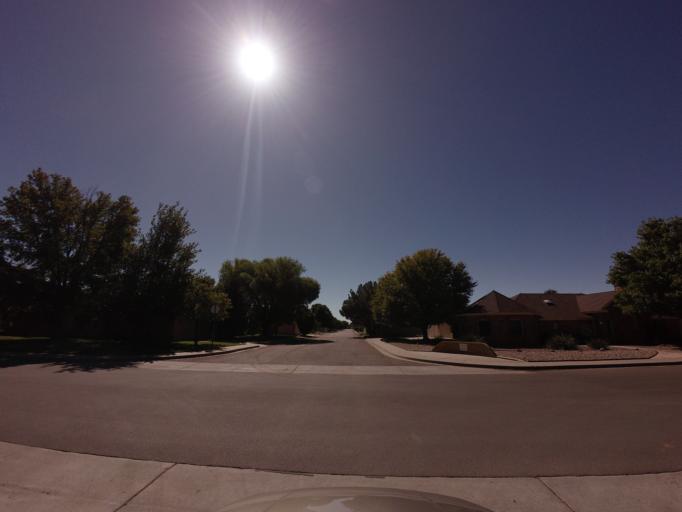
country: US
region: New Mexico
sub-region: Curry County
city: Clovis
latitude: 34.4218
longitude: -103.1743
